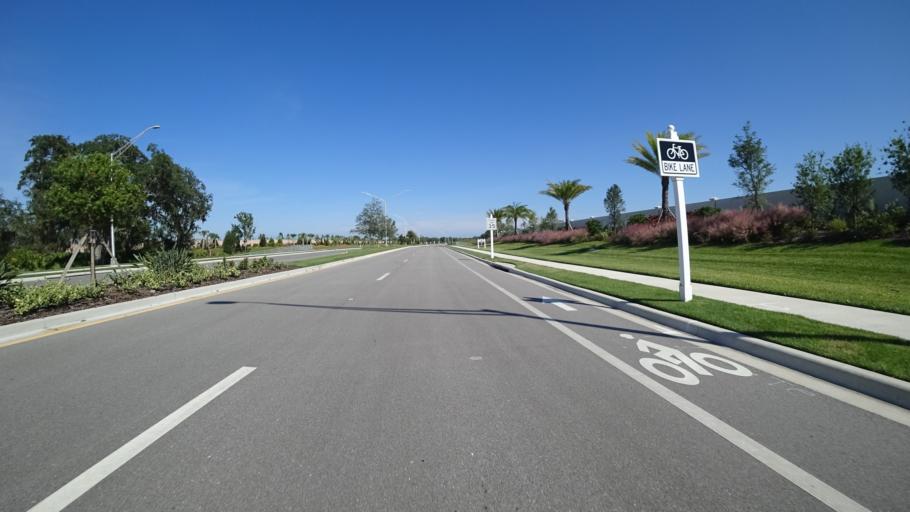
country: US
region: Florida
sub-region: Sarasota County
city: The Meadows
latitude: 27.4017
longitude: -82.3620
